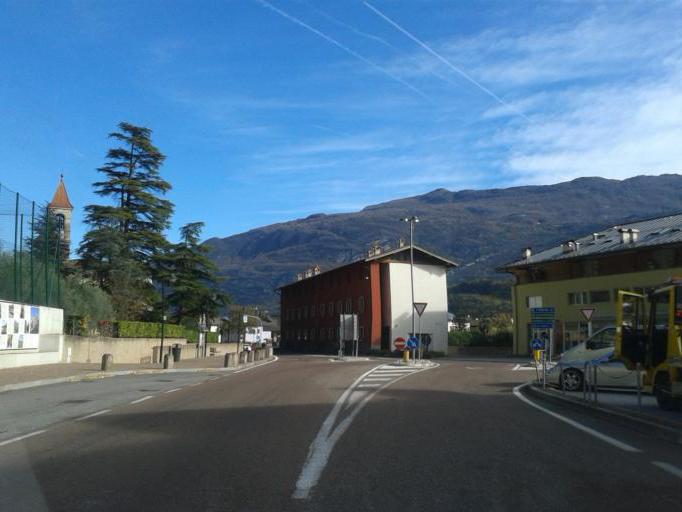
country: IT
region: Trentino-Alto Adige
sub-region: Provincia di Trento
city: Pietramurata
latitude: 46.0471
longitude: 10.9517
